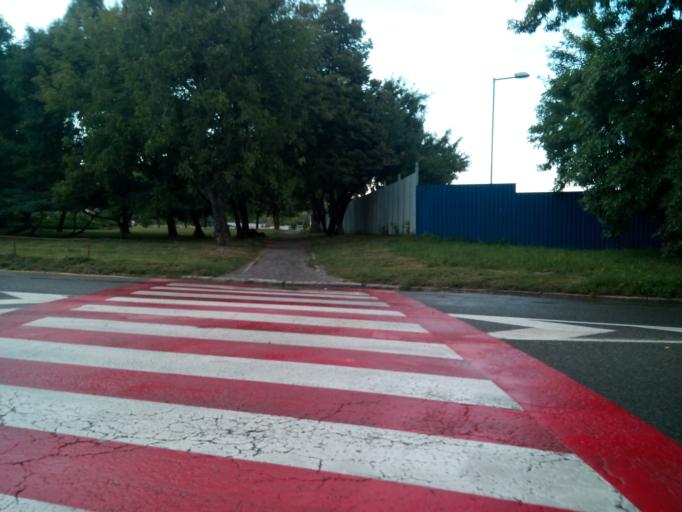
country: SK
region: Kosicky
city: Kosice
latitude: 48.7417
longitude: 21.2492
